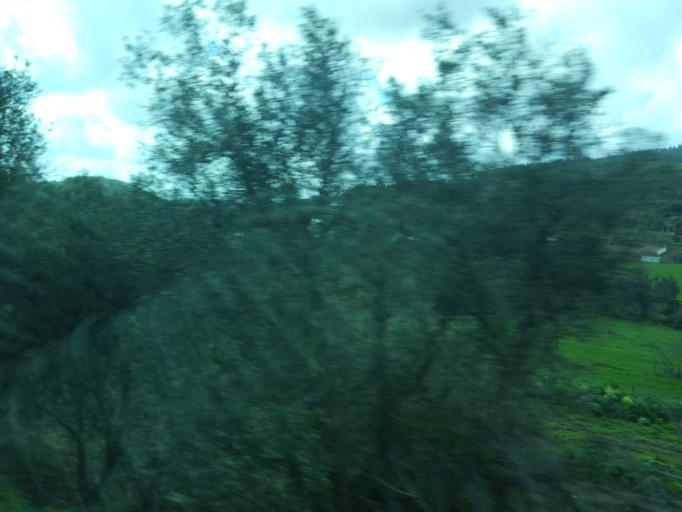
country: PT
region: Faro
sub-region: Monchique
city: Monchique
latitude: 37.2990
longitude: -8.5645
